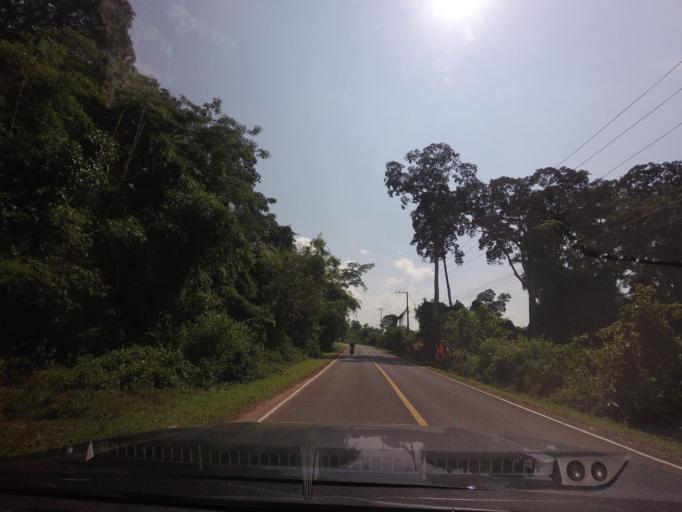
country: TH
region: Nan
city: Bo Kluea
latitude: 19.0655
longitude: 101.1624
